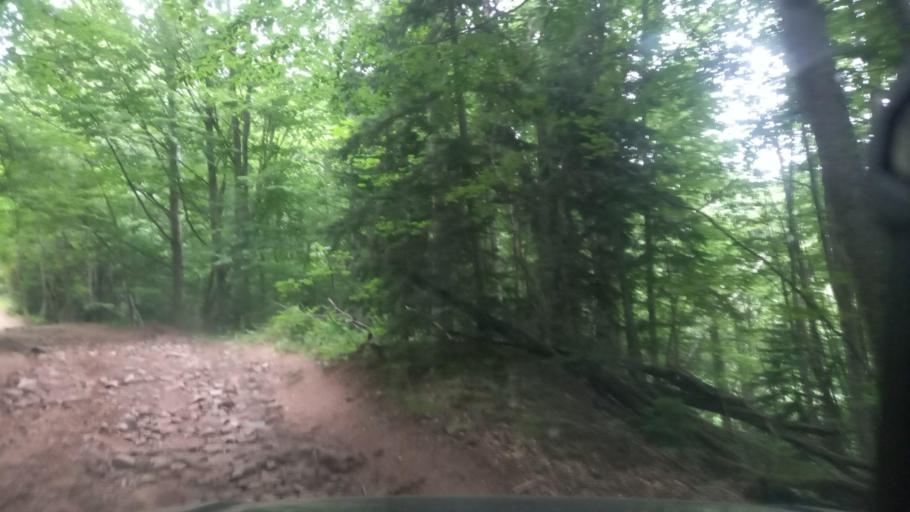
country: RU
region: Karachayevo-Cherkesiya
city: Kurdzhinovo
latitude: 43.8089
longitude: 40.8634
